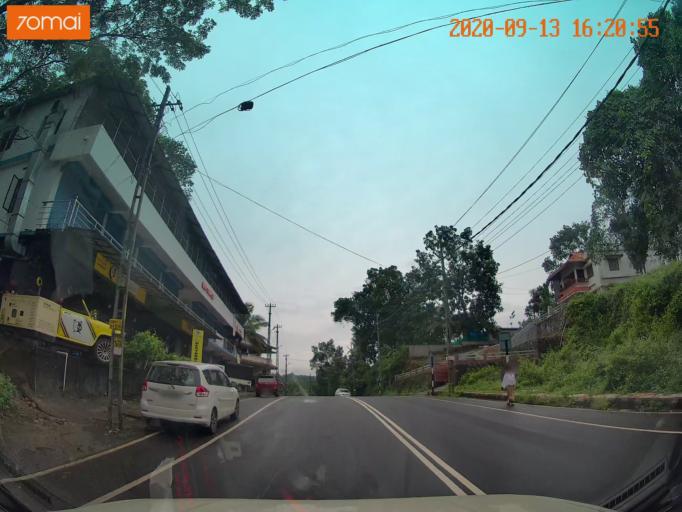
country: IN
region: Kerala
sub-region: Kottayam
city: Lalam
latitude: 9.7055
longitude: 76.6638
